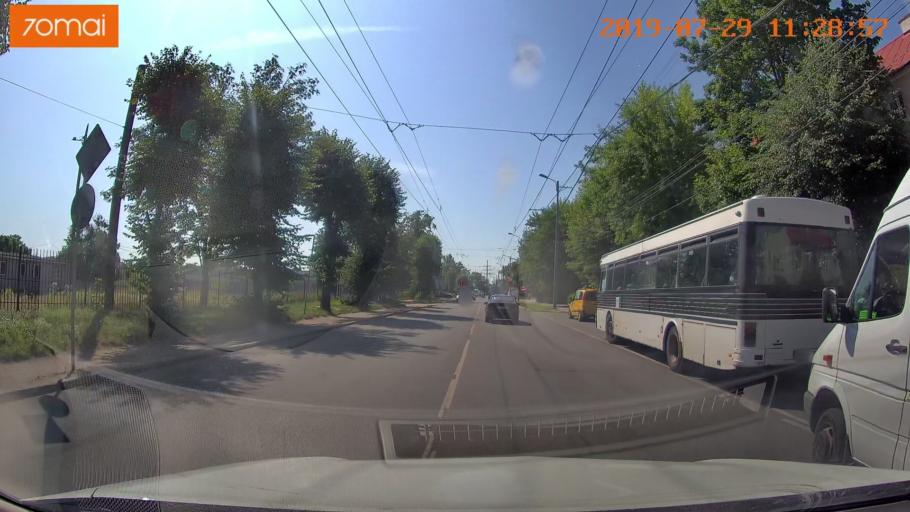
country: RU
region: Kaliningrad
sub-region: Gorod Kaliningrad
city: Kaliningrad
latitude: 54.6862
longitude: 20.5331
